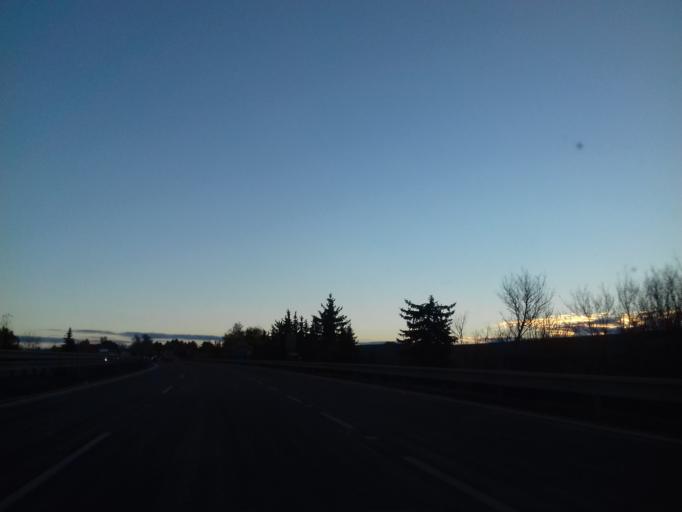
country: CZ
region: South Moravian
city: Rousinov
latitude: 49.1884
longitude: 16.8744
